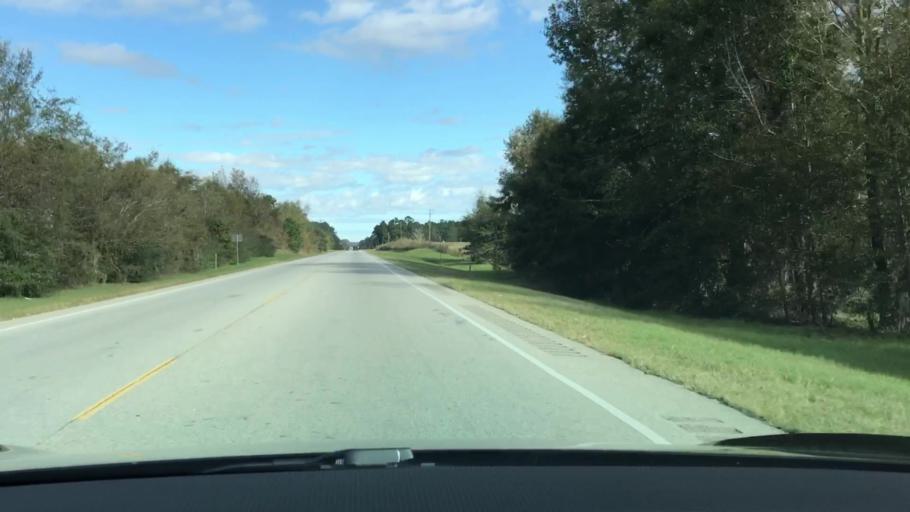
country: US
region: Georgia
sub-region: Jefferson County
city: Wadley
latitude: 32.9281
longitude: -82.3970
